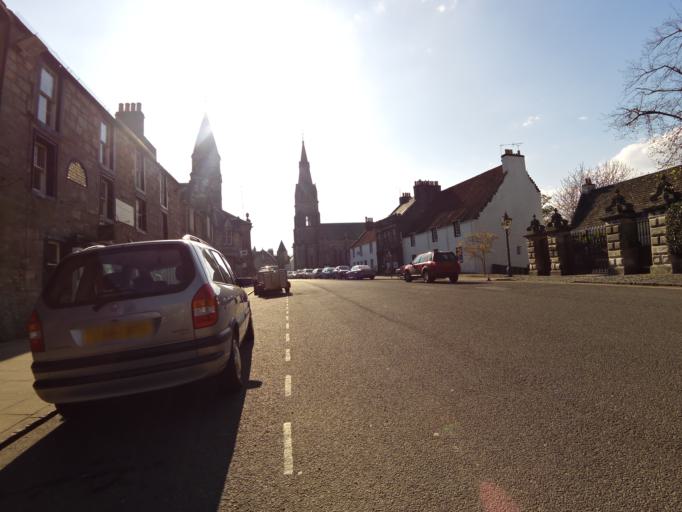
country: GB
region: Scotland
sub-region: Fife
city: Falkland
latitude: 56.2534
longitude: -3.2066
